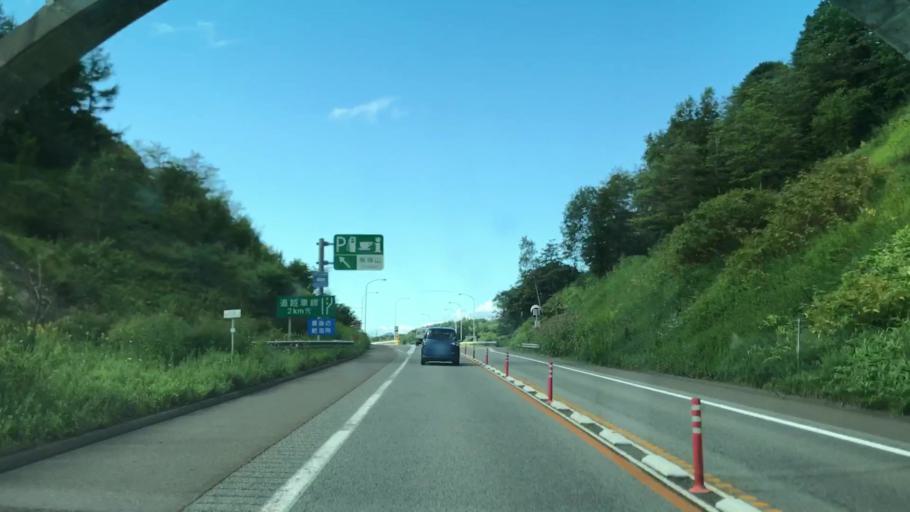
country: JP
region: Hokkaido
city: Date
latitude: 42.4618
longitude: 140.9108
